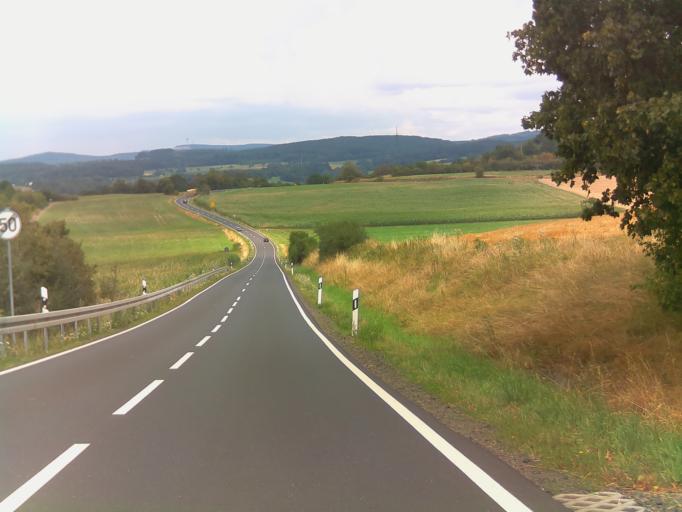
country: DE
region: Hesse
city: Gedern
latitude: 50.4072
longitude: 9.1949
